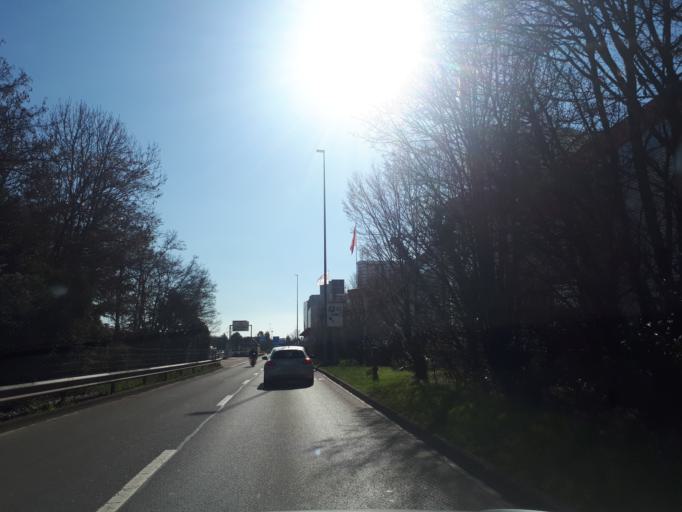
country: CH
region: Geneva
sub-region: Geneva
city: Le Grand-Saconnex
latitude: 46.2347
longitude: 6.1147
